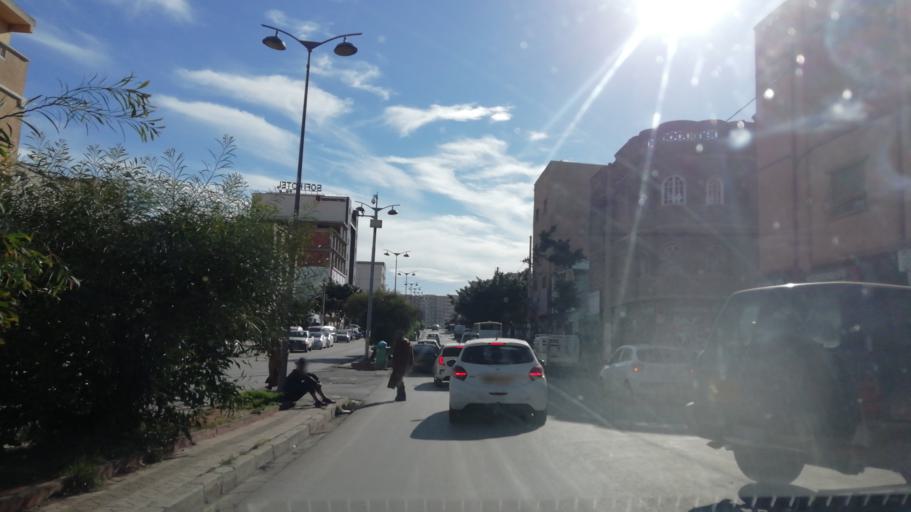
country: DZ
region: Oran
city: Oran
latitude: 35.6941
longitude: -0.6199
